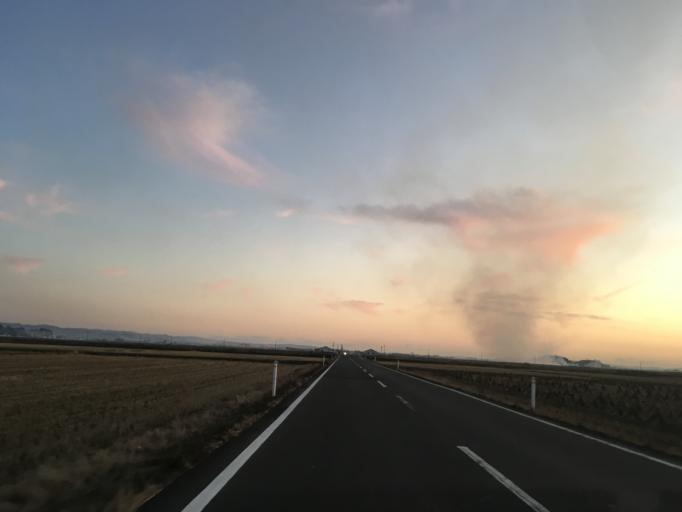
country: JP
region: Iwate
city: Ichinoseki
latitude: 38.7508
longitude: 141.2367
